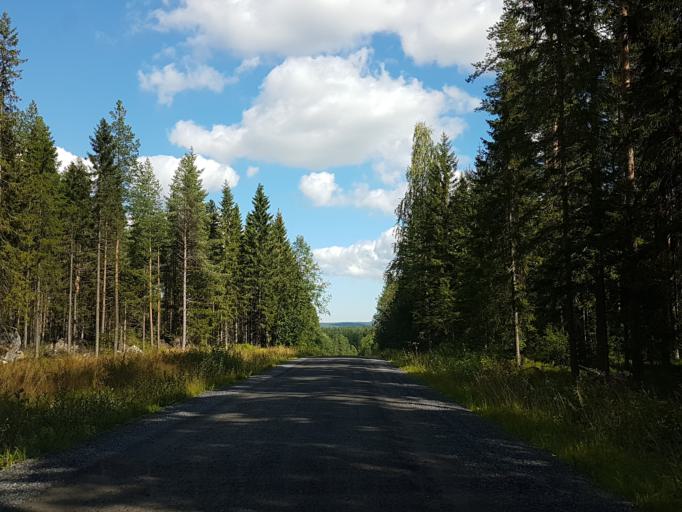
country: SE
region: Vaesterbotten
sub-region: Skelleftea Kommun
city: Burtraesk
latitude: 64.2945
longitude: 20.5099
